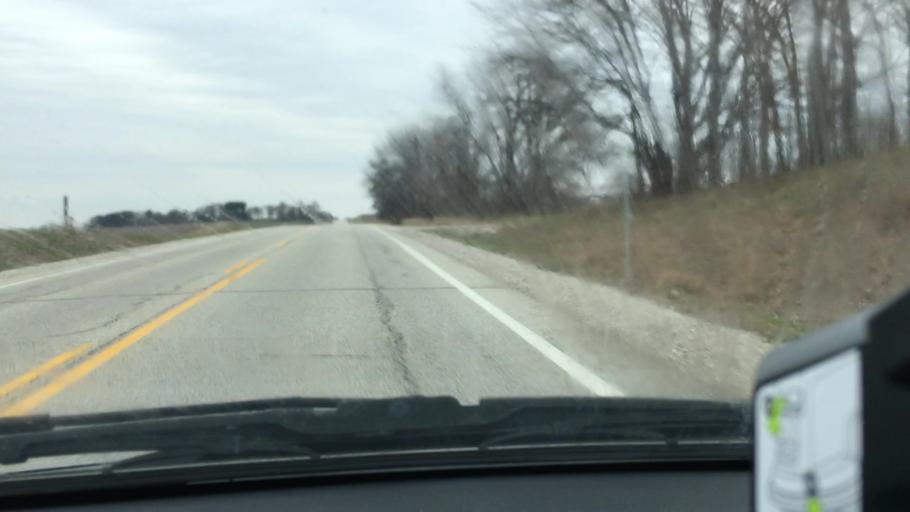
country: US
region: Indiana
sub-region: Greene County
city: Bloomfield
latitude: 38.9548
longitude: -87.0167
